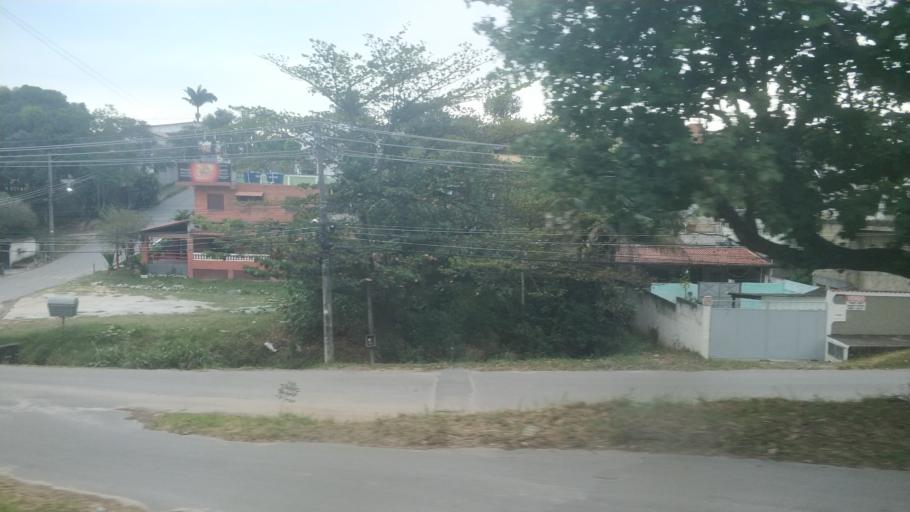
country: BR
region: Rio de Janeiro
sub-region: Seropedica
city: Seropedica
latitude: -22.7501
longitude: -43.6969
